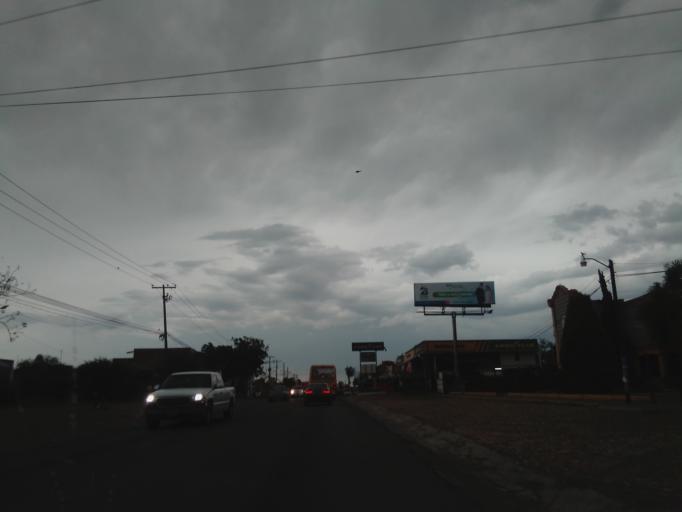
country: MX
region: Guanajuato
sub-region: Dolores Hidalgo Cuna de la Independencia Nacional
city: Dolores Hidalgo Cuna de la Independencia Nacional
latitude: 21.1574
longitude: -100.9238
